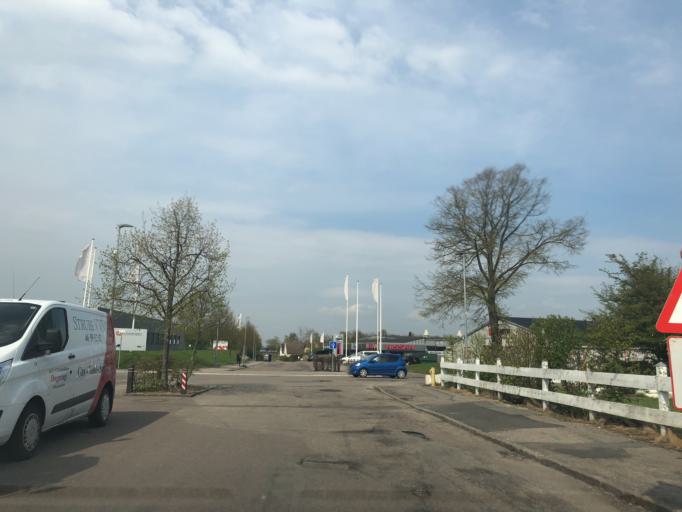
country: DK
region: Zealand
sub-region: Roskilde Kommune
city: Roskilde
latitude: 55.6434
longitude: 12.1109
